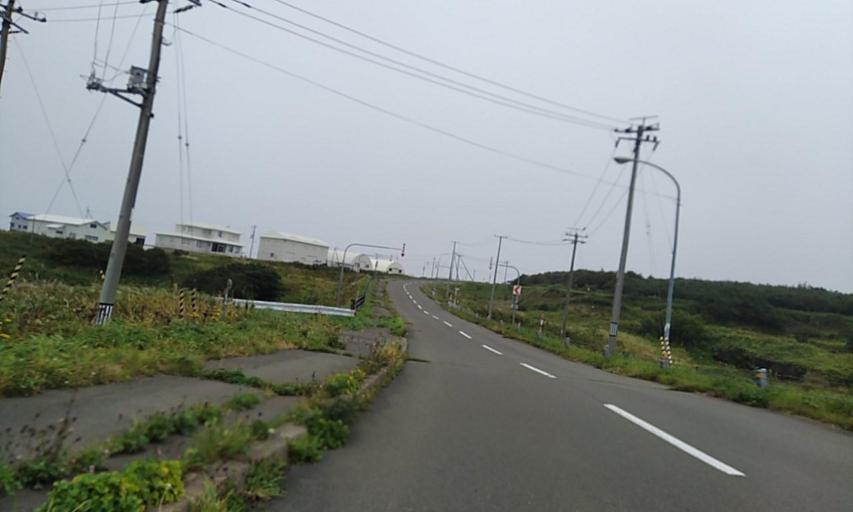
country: JP
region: Hokkaido
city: Nemuro
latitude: 43.3841
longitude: 145.7896
